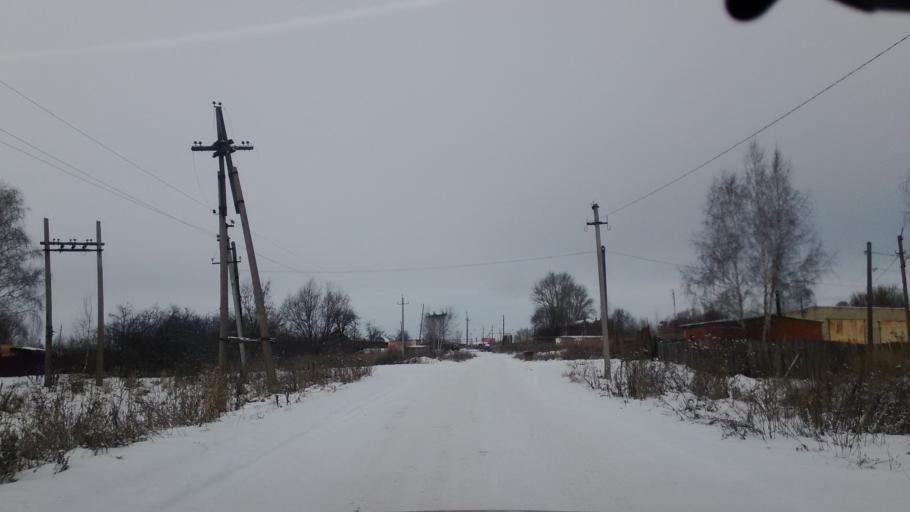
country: RU
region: Tula
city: Bogoroditsk
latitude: 53.7654
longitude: 38.1014
